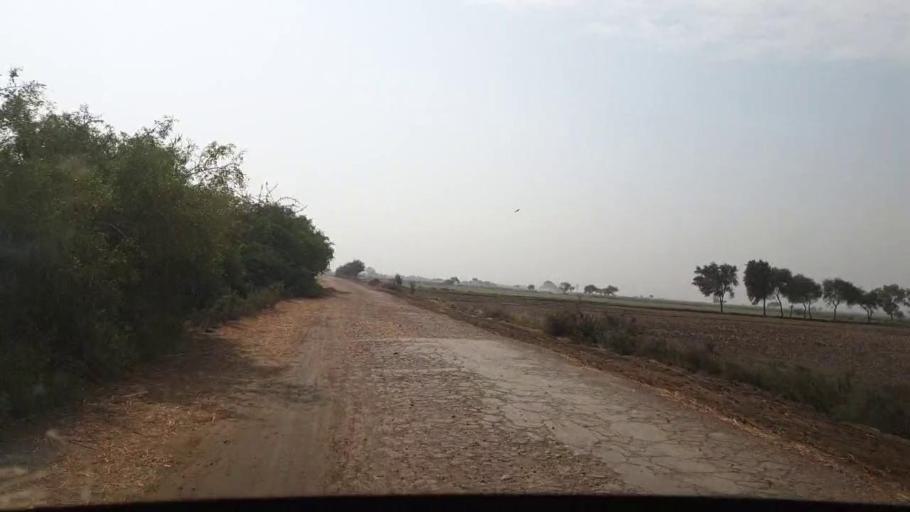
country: PK
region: Sindh
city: Chuhar Jamali
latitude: 24.3844
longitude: 67.9387
